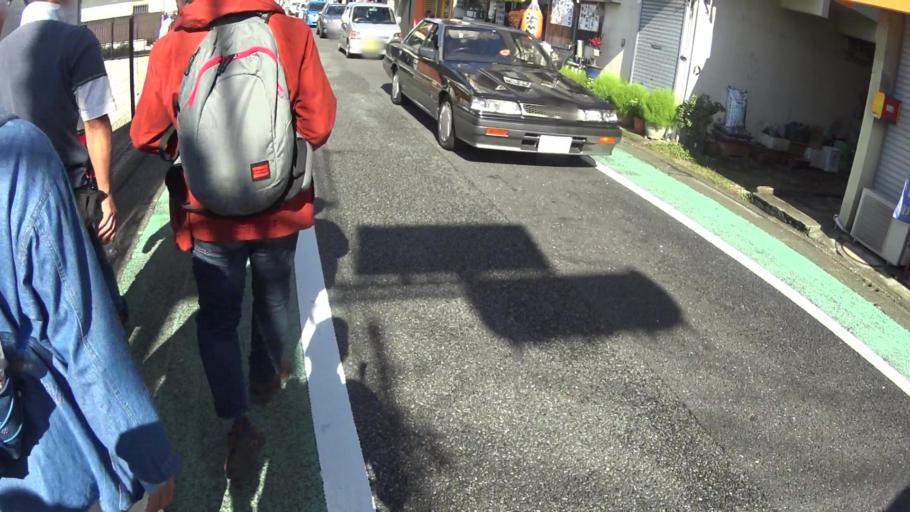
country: JP
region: Tokyo
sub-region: Machida-shi
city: Machida
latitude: 35.5495
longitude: 139.4476
